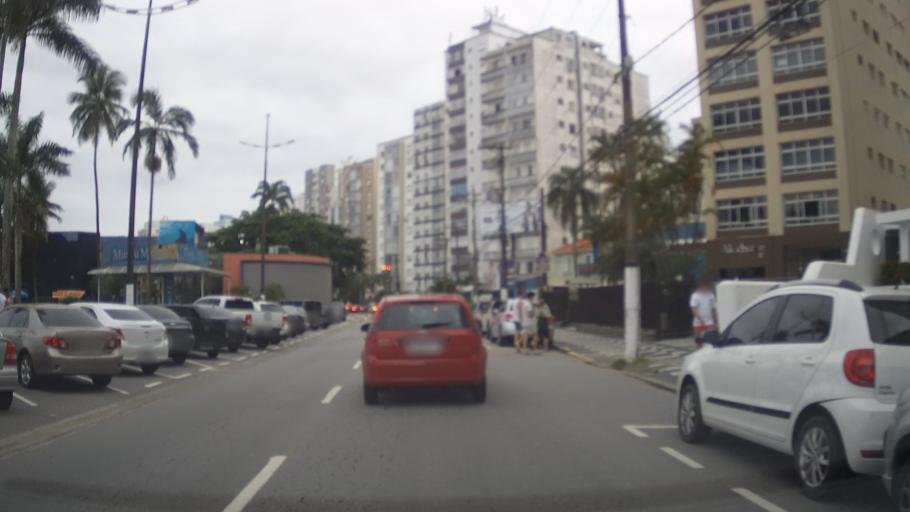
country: BR
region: Sao Paulo
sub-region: Santos
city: Santos
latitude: -23.9872
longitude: -46.3078
